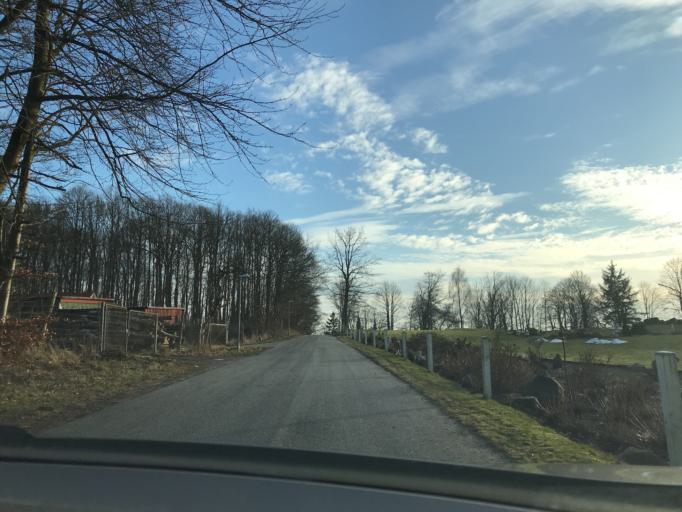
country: DK
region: South Denmark
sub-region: Vejle Kommune
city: Vejle
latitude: 55.6897
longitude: 9.5311
